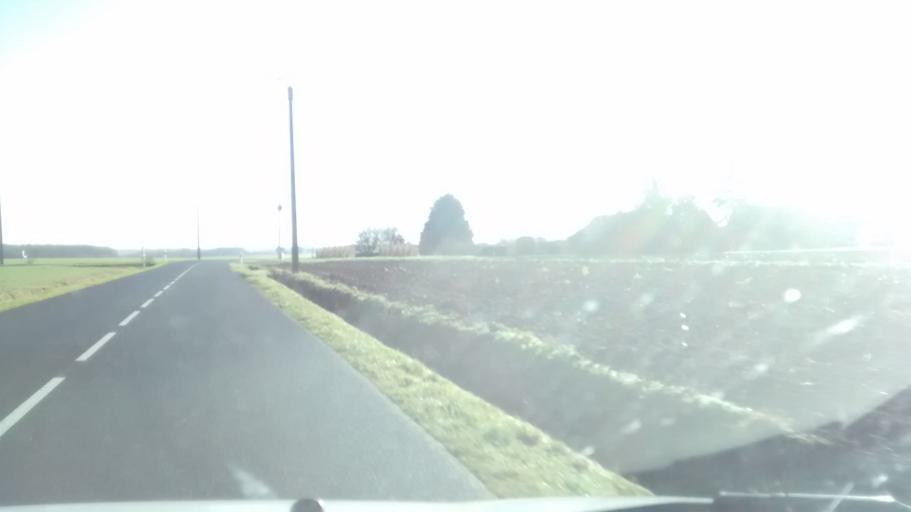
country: FR
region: Centre
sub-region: Departement d'Indre-et-Loire
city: Monnaie
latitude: 47.4902
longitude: 0.8339
